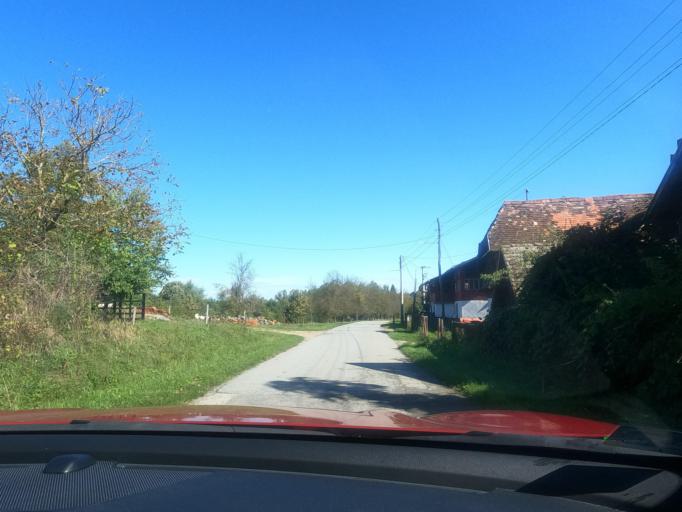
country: HR
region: Sisacko-Moslavacka
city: Petrinja
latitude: 45.3479
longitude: 16.2140
